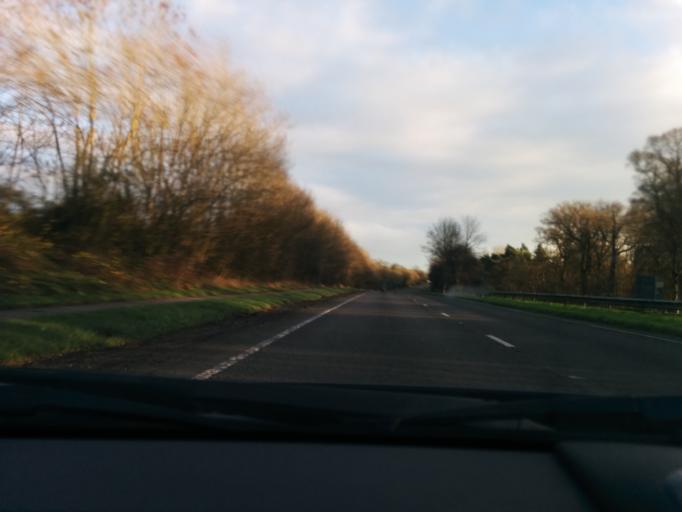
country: GB
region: England
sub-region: Oxfordshire
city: Wheatley
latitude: 51.7589
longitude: -1.1528
